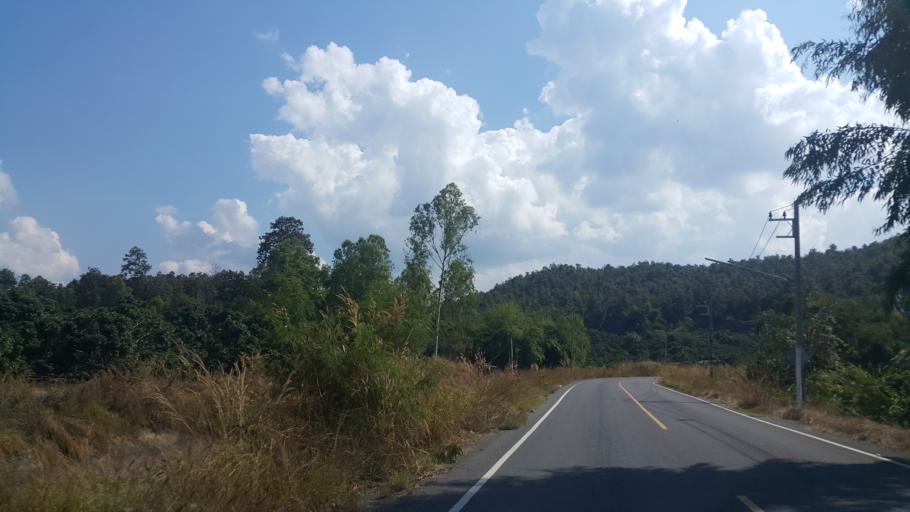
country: TH
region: Lamphun
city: Ban Thi
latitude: 18.6356
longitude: 99.1610
